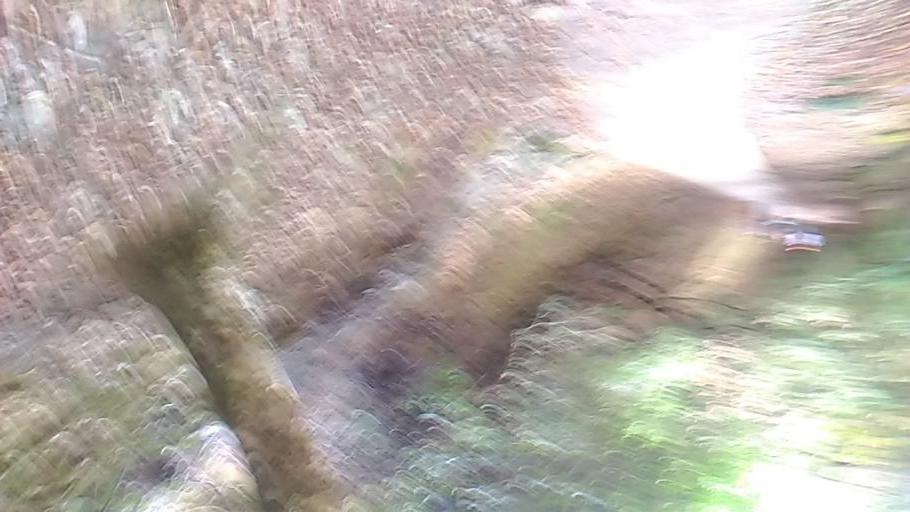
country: TW
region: Taiwan
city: Daxi
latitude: 24.4101
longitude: 121.3027
